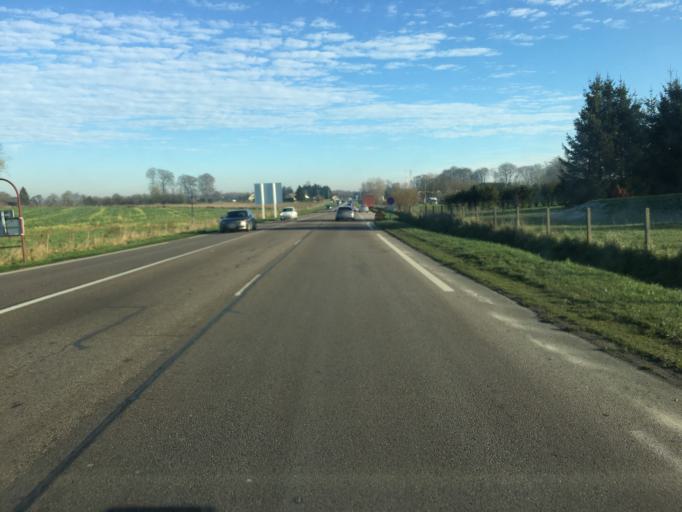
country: FR
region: Haute-Normandie
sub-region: Departement de la Seine-Maritime
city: Sainte-Marie-des-Champs
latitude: 49.6259
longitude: 0.7903
